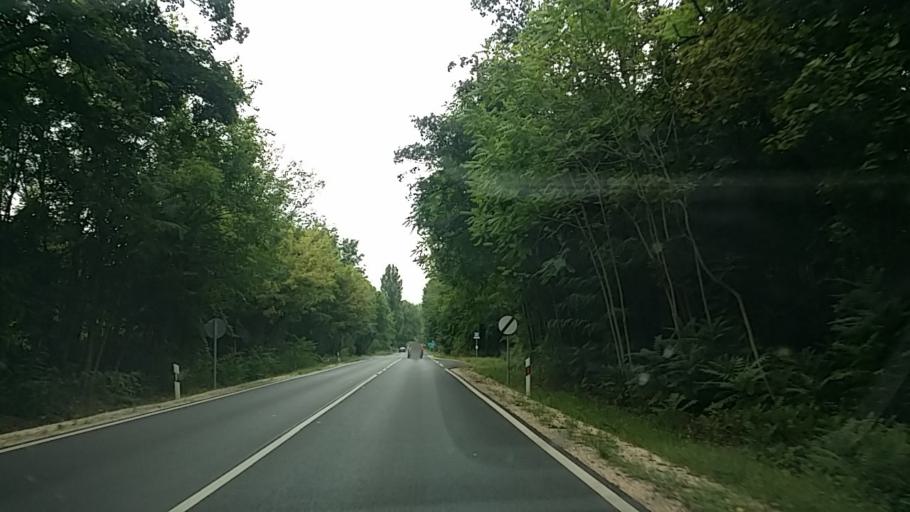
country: HU
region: Komarom-Esztergom
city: Acs
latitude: 47.7252
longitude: 18.0454
